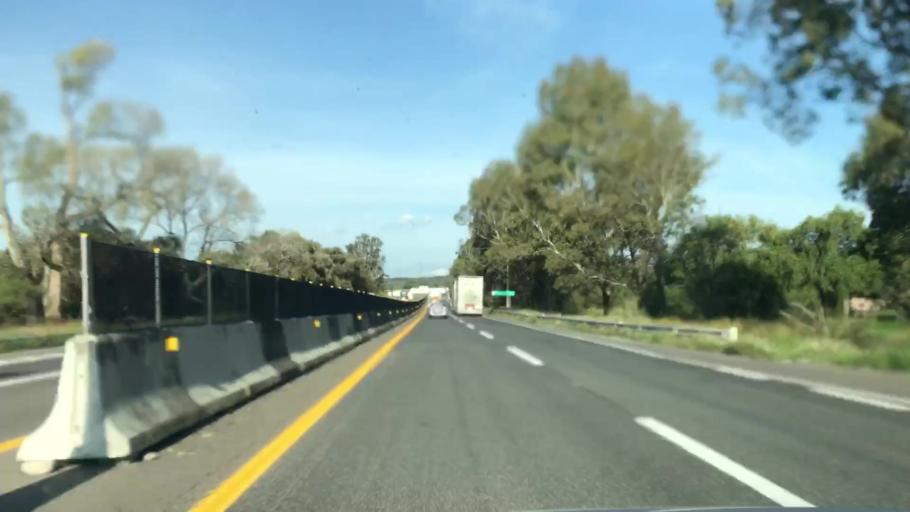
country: MX
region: Jalisco
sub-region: Lagos de Moreno
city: Cristeros [Fraccionamiento]
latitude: 21.3176
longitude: -102.0486
